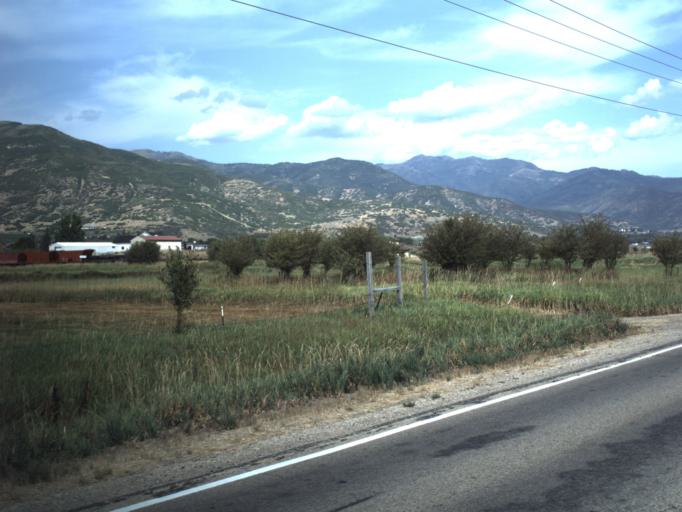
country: US
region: Utah
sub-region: Wasatch County
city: Midway
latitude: 40.4851
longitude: -111.4719
